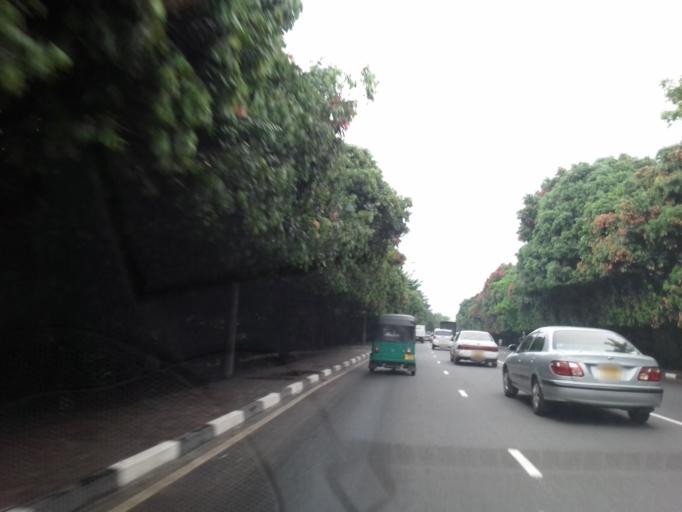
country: LK
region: Western
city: Battaramulla South
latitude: 6.8968
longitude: 79.9145
